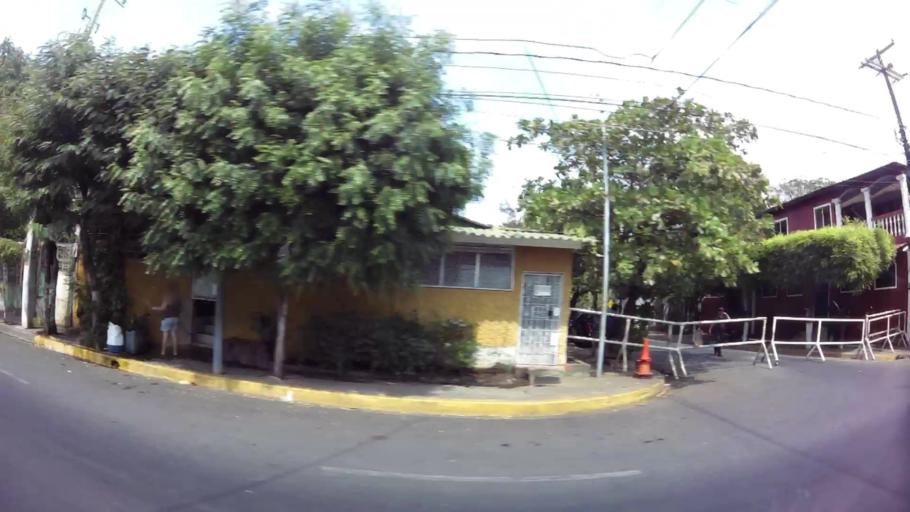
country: NI
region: Managua
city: Managua
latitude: 12.1452
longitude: -86.2879
